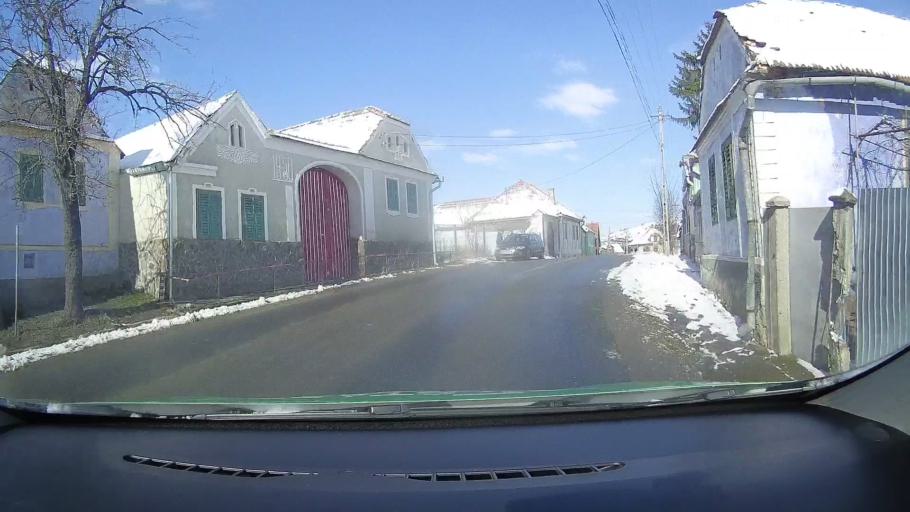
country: RO
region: Sibiu
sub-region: Comuna Barghis
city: Barghis
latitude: 45.9881
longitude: 24.4834
